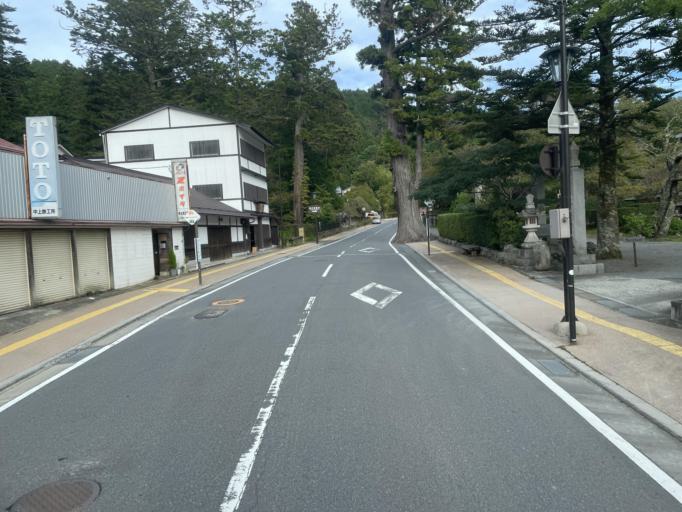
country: JP
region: Wakayama
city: Koya
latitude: 34.2165
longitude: 135.5825
